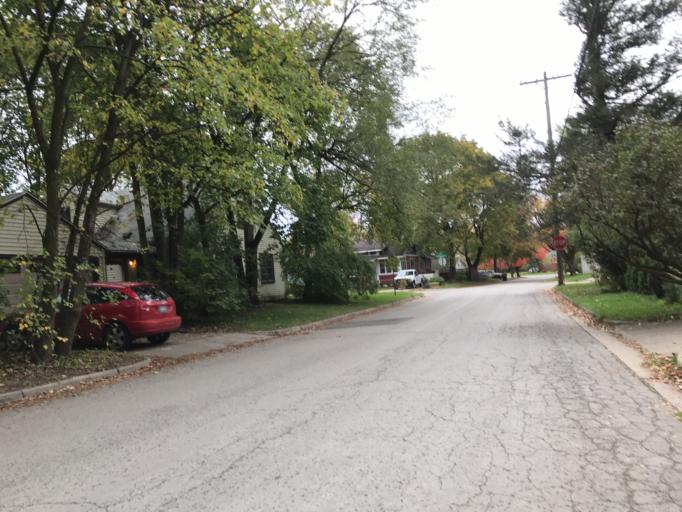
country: US
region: Michigan
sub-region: Washtenaw County
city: Ann Arbor
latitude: 42.2525
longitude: -83.7282
